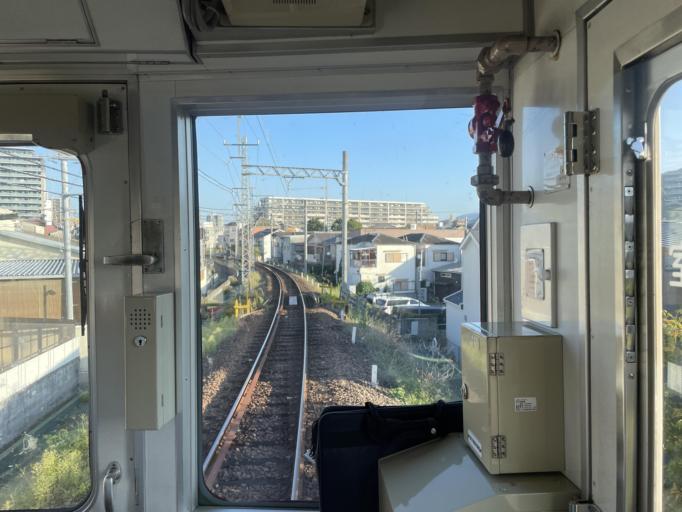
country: JP
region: Osaka
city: Kashihara
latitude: 34.5833
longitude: 135.6251
